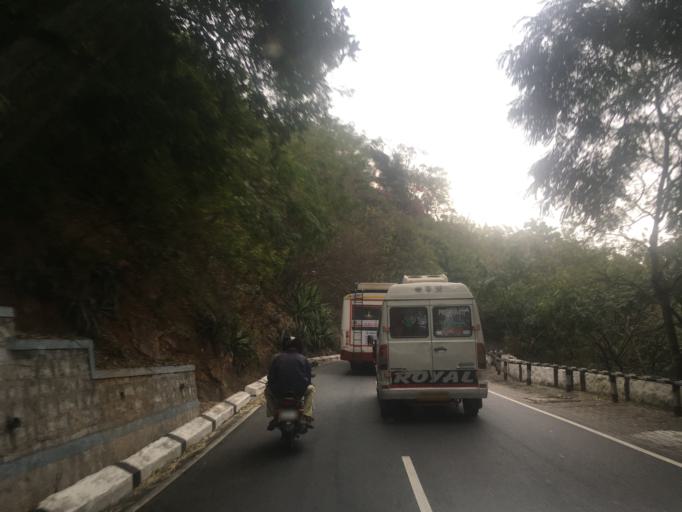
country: IN
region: Andhra Pradesh
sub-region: Chittoor
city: Tirumala
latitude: 13.6656
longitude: 79.3519
